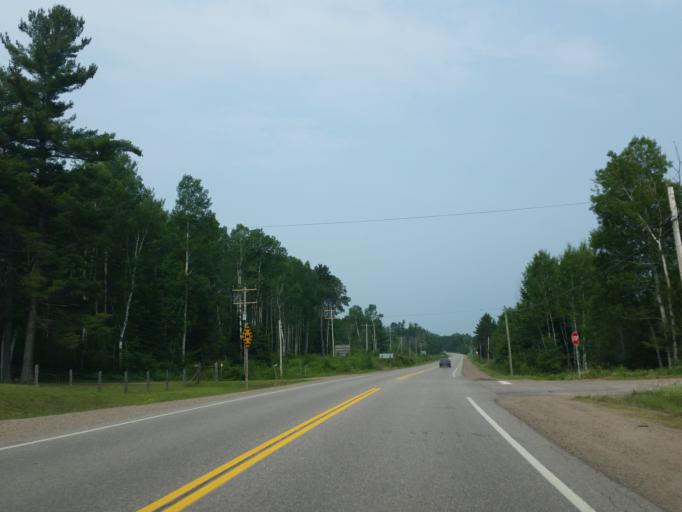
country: CA
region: Ontario
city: Petawawa
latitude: 45.5009
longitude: -77.6015
